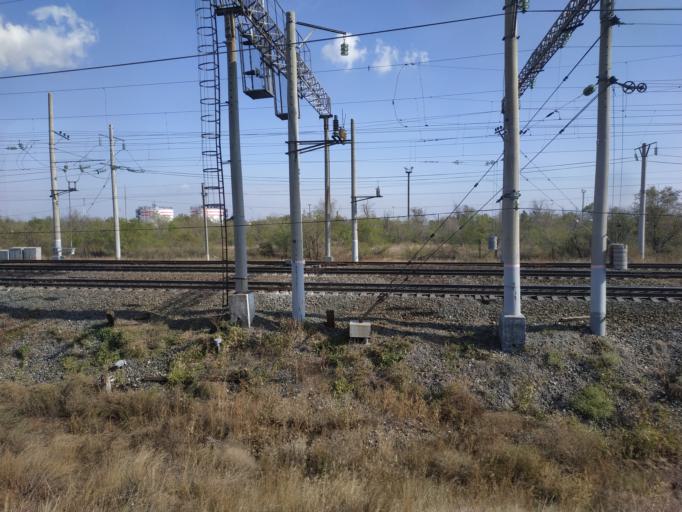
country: RU
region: Volgograd
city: Gumrak
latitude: 48.7931
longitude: 44.3650
